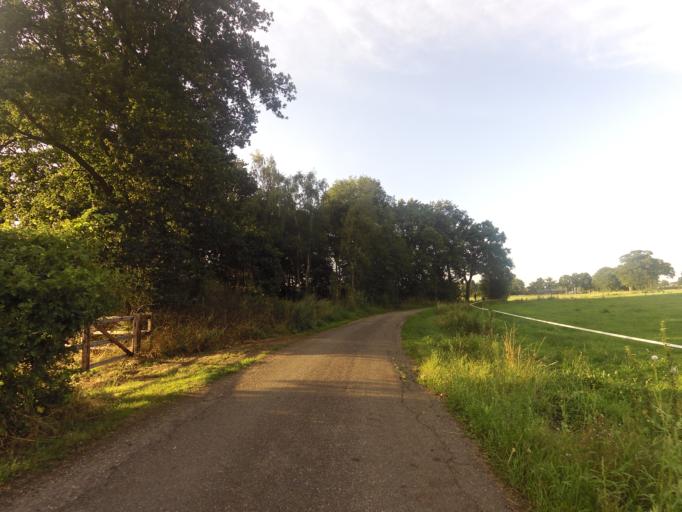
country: NL
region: Gelderland
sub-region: Oude IJsselstreek
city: Varsseveld
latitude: 51.9128
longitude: 6.4743
